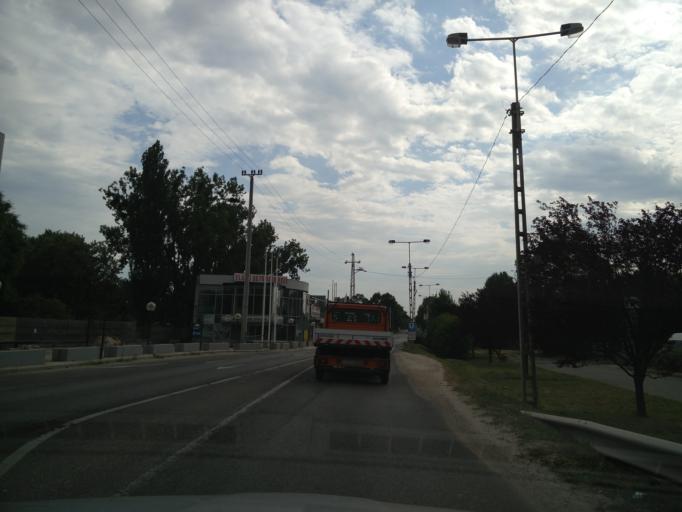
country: HU
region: Pest
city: Budakeszi
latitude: 47.5027
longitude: 18.9206
